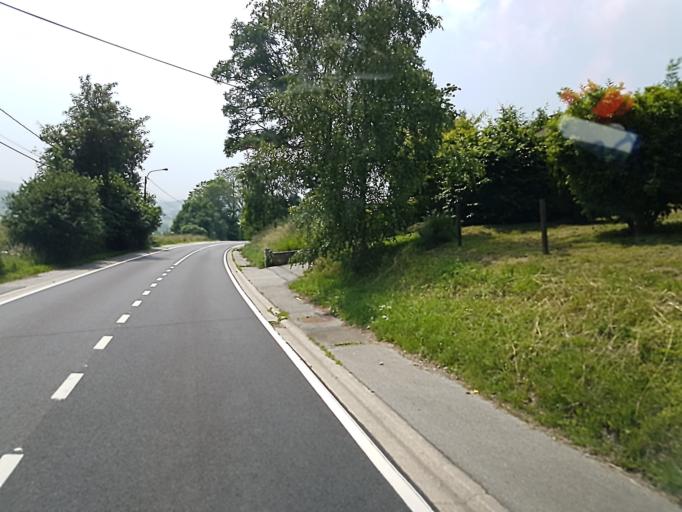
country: BE
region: Wallonia
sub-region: Province de Liege
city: Lierneux
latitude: 50.3303
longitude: 5.7710
